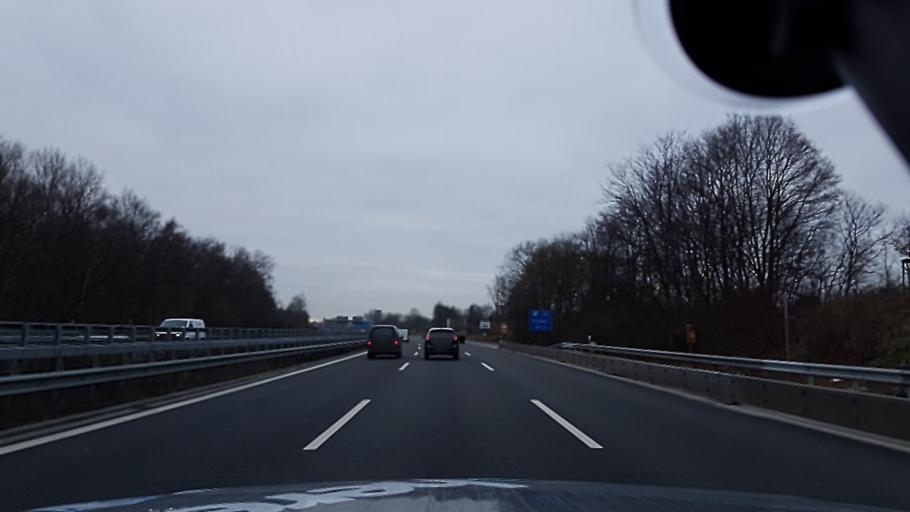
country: DE
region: Schleswig-Holstein
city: Oststeinbek
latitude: 53.5563
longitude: 10.1530
